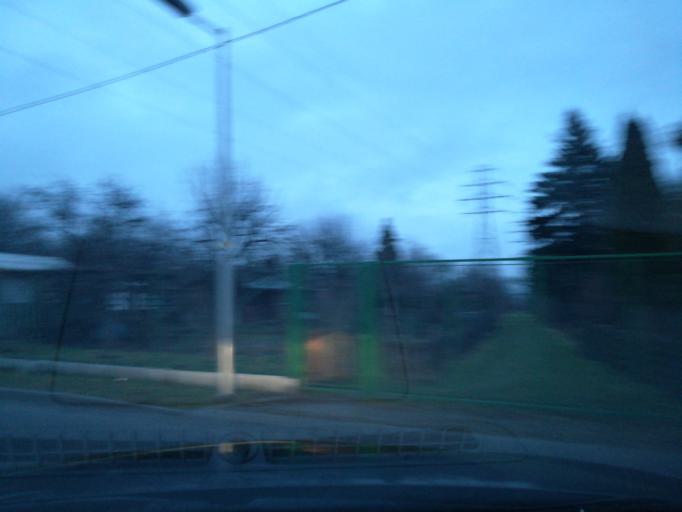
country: PL
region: Subcarpathian Voivodeship
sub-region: Rzeszow
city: Rzeszow
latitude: 50.0172
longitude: 22.0139
